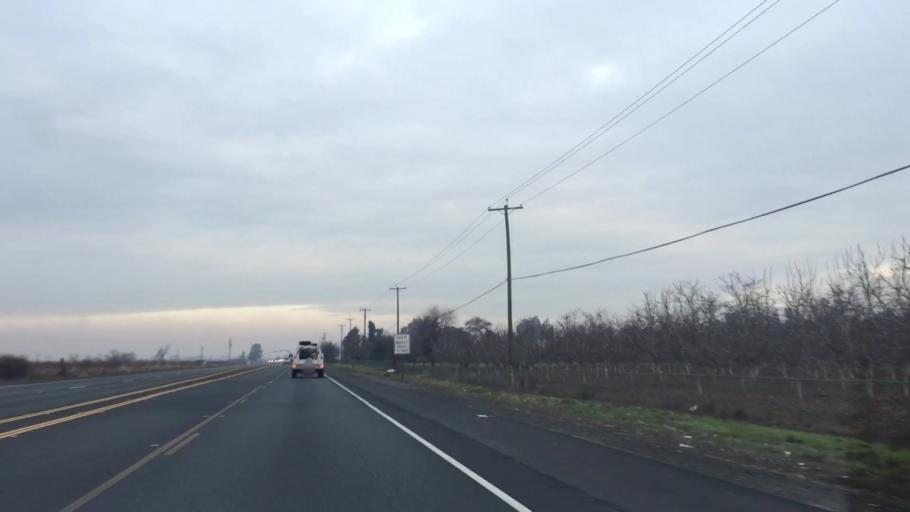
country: US
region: California
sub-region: Butte County
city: Gridley
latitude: 39.3591
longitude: -121.6058
